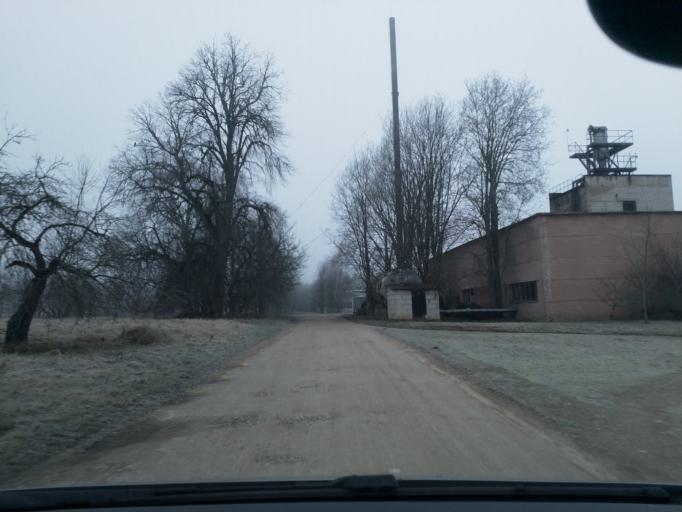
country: LV
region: Kuldigas Rajons
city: Kuldiga
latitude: 56.8410
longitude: 21.9433
